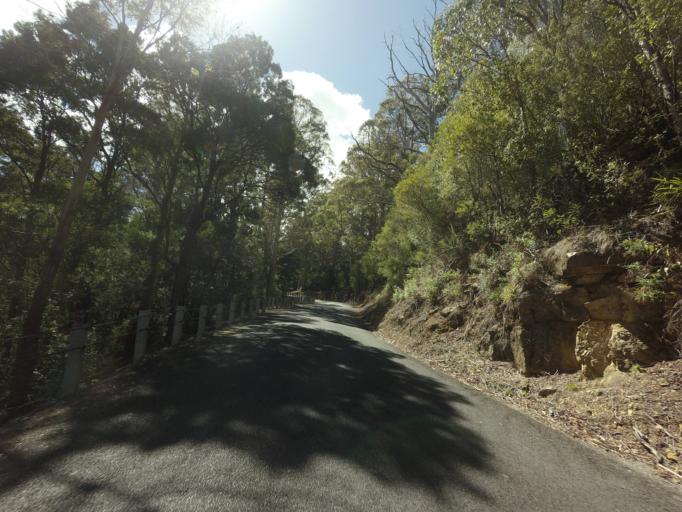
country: AU
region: Tasmania
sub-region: Break O'Day
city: St Helens
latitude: -41.6386
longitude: 148.2425
